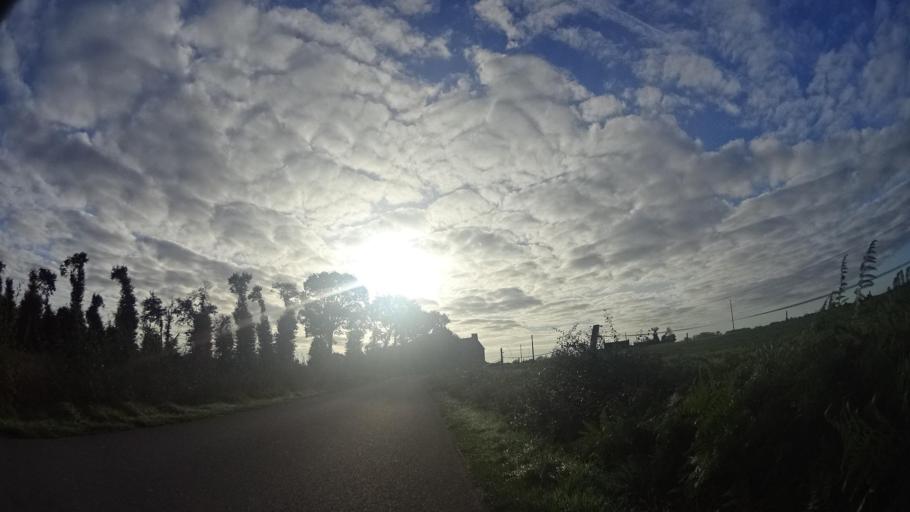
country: FR
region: Brittany
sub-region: Departement des Cotes-d'Armor
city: Evran
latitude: 48.3673
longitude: -1.9576
